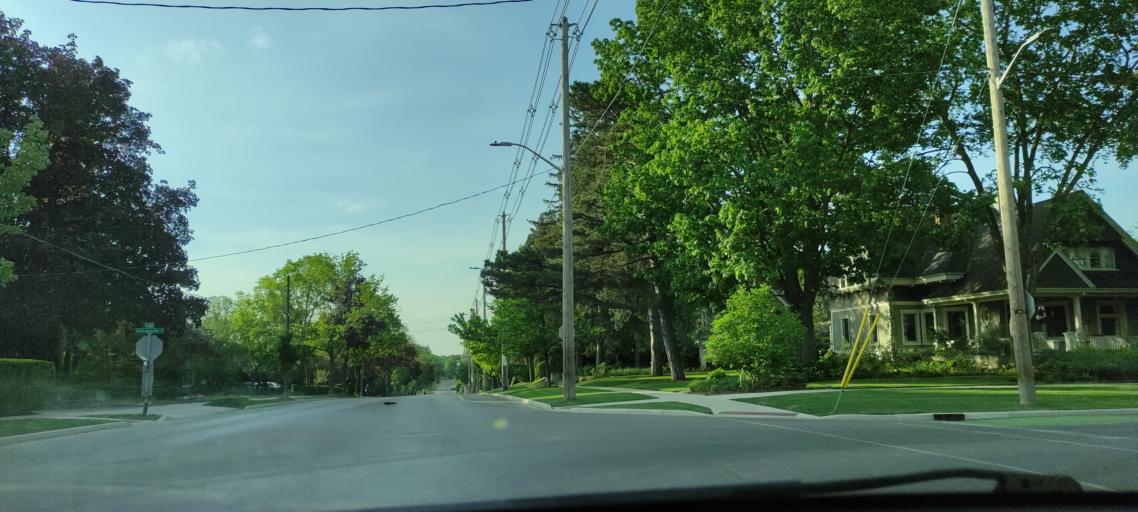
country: CA
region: Ontario
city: London
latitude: 43.0010
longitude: -81.2584
